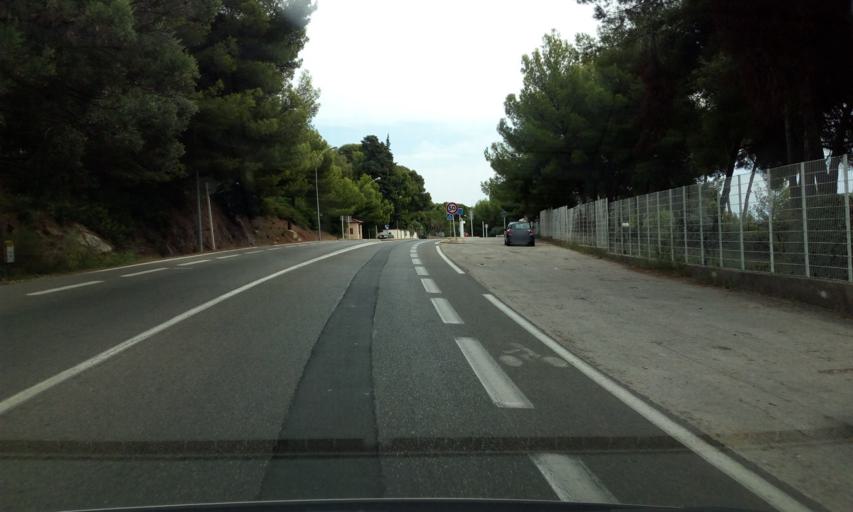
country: FR
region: Provence-Alpes-Cote d'Azur
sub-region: Departement du Var
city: Carqueiranne
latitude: 43.0849
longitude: 6.1077
